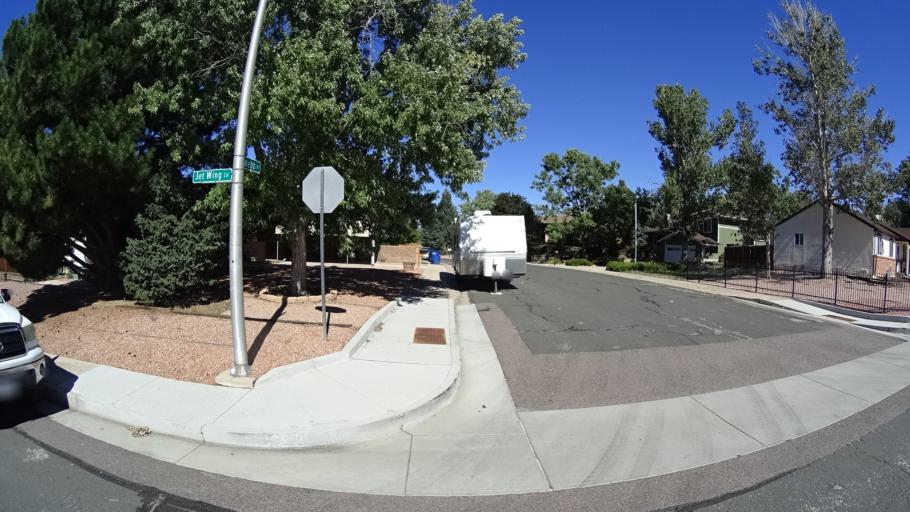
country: US
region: Colorado
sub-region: El Paso County
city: Stratmoor
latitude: 38.8125
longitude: -104.7357
